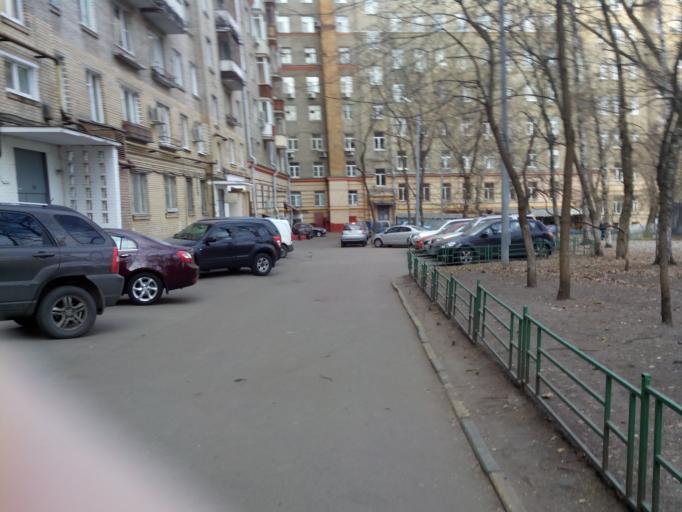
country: RU
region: Moscow
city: Lefortovo
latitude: 55.7767
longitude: 37.7059
